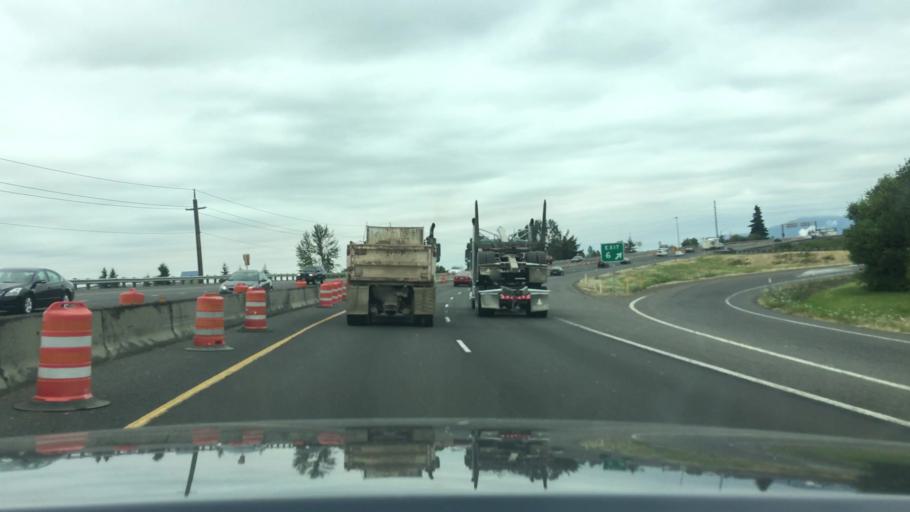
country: US
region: Oregon
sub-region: Lane County
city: Eugene
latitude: 44.0939
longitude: -123.1704
